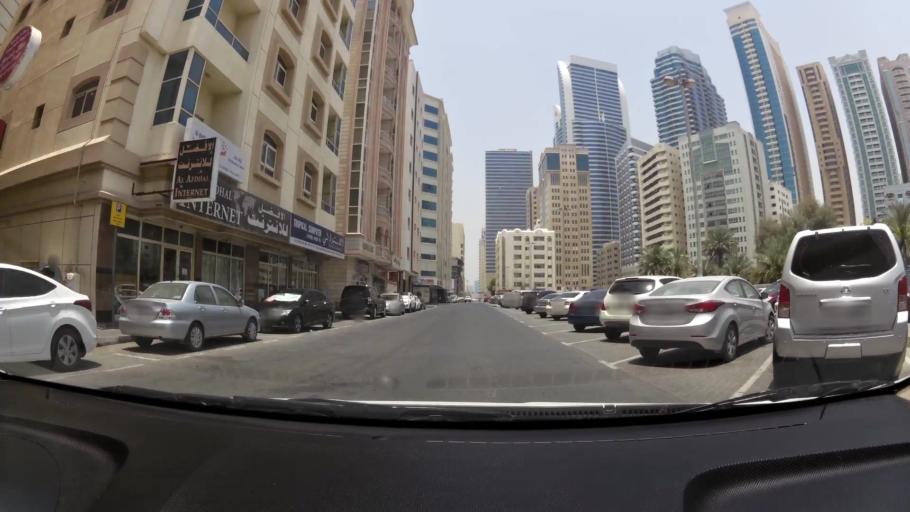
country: AE
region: Ash Shariqah
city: Sharjah
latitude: 25.3341
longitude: 55.3728
